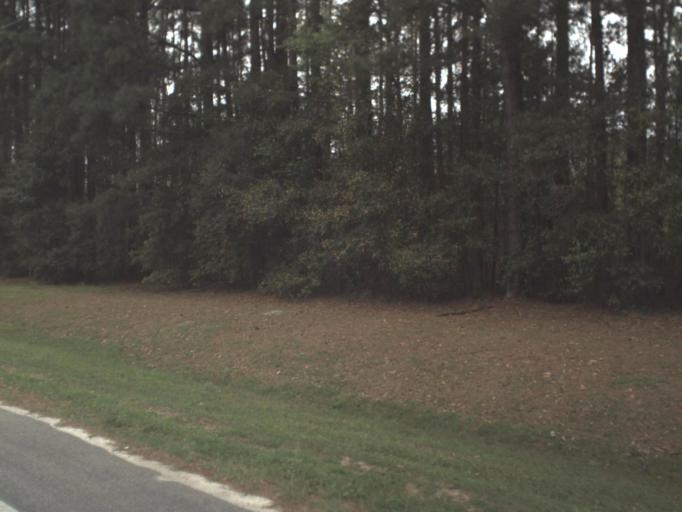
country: US
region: Florida
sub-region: Gulf County
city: Wewahitchka
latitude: 30.0930
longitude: -85.1963
